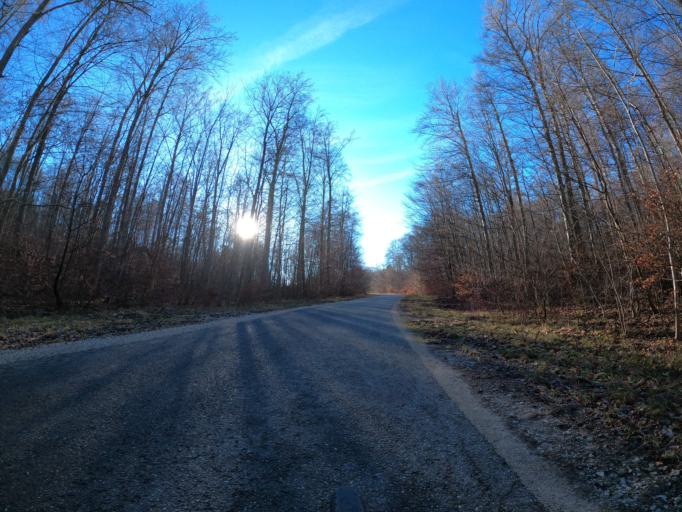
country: DE
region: Baden-Wuerttemberg
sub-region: Tuebingen Region
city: Sankt Johann
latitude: 48.4371
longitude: 9.2960
